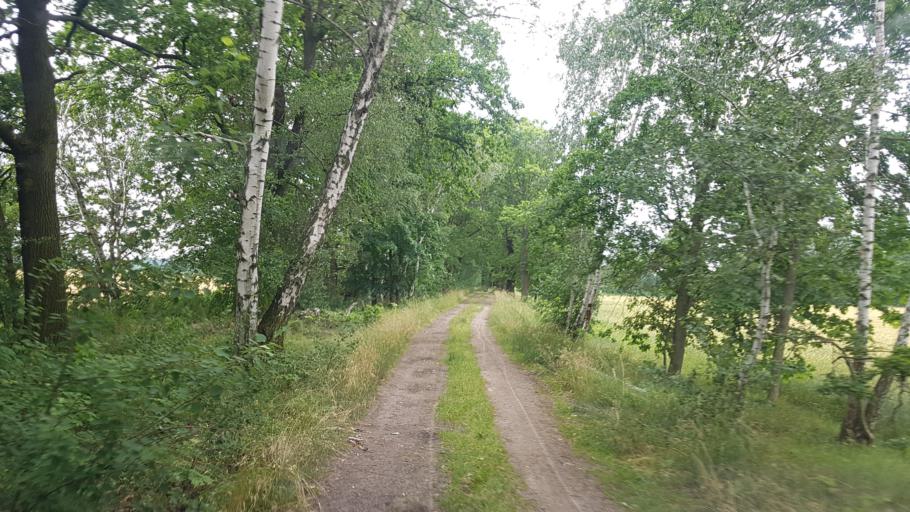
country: DE
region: Brandenburg
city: Grossthiemig
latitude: 51.4086
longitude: 13.6651
